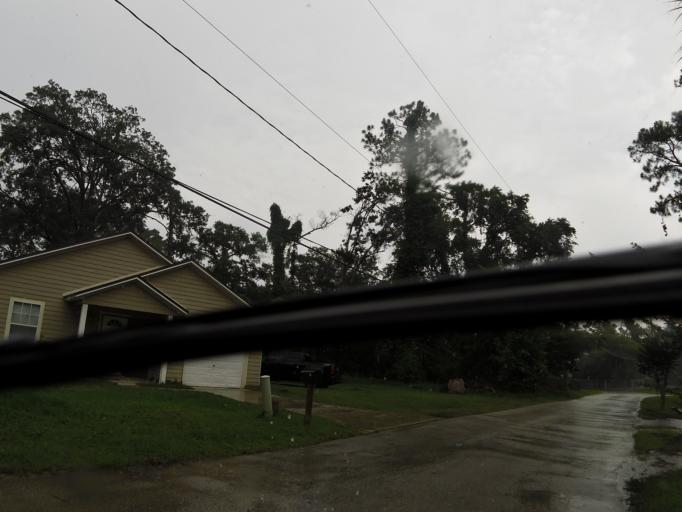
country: US
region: Florida
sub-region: Duval County
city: Jacksonville
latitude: 30.3024
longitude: -81.6401
